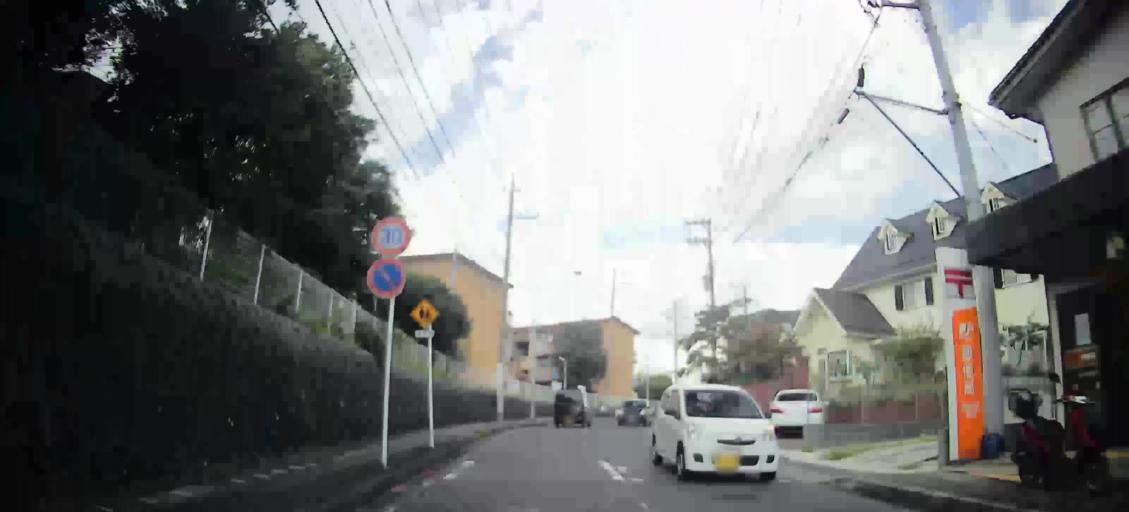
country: JP
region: Kanagawa
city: Yokohama
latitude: 35.4631
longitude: 139.5603
